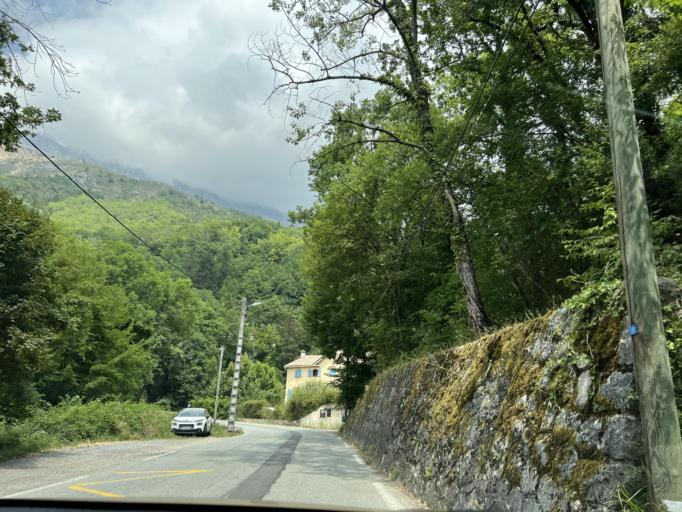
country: FR
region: Provence-Alpes-Cote d'Azur
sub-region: Departement des Alpes-Maritimes
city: Tourrettes-sur-Loup
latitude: 43.7932
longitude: 6.9745
